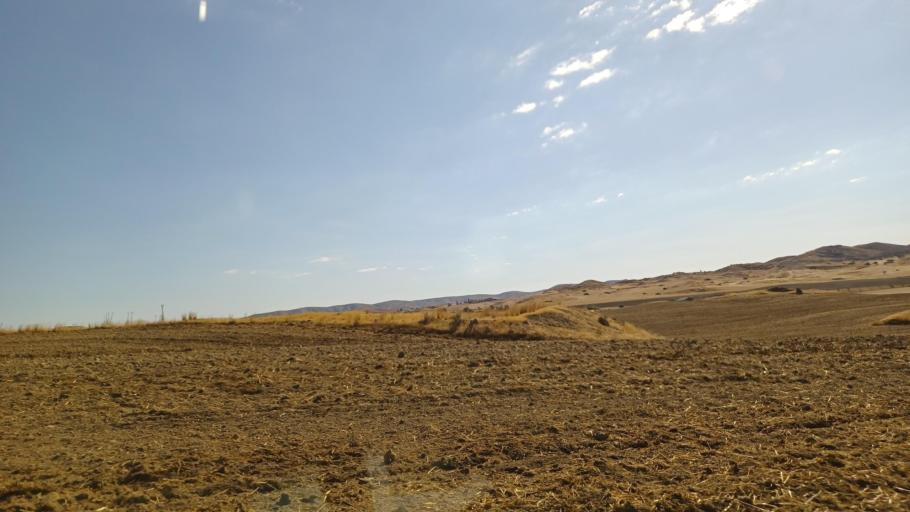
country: CY
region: Larnaka
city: Troulloi
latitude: 35.0026
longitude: 33.5932
